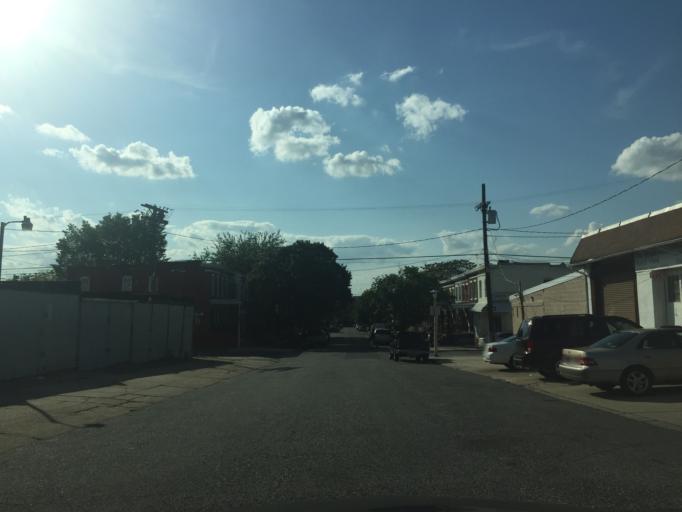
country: US
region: Maryland
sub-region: City of Baltimore
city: Baltimore
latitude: 39.3152
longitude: -76.5975
